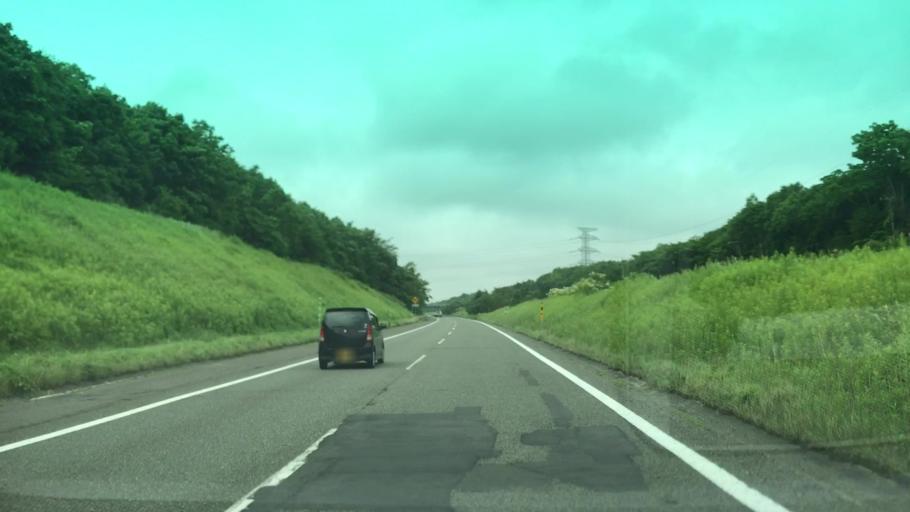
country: JP
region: Hokkaido
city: Chitose
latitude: 42.7342
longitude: 141.6526
